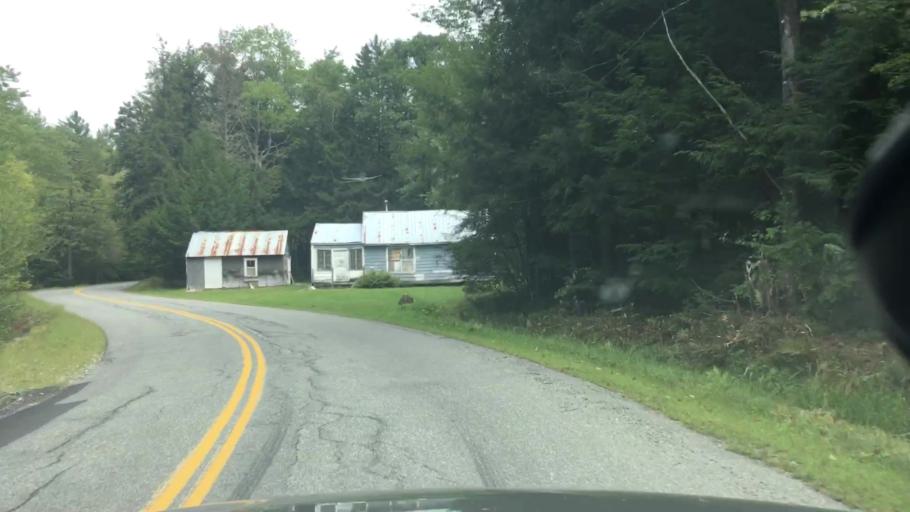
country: US
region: Massachusetts
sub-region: Franklin County
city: Colrain
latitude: 42.7979
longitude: -72.7694
